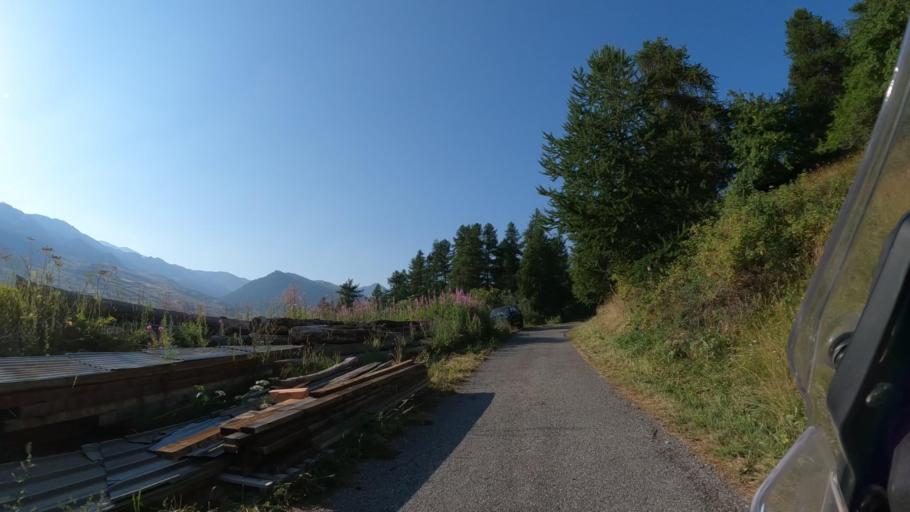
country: FR
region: Provence-Alpes-Cote d'Azur
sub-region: Departement des Hautes-Alpes
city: Guillestre
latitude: 44.6022
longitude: 6.6819
